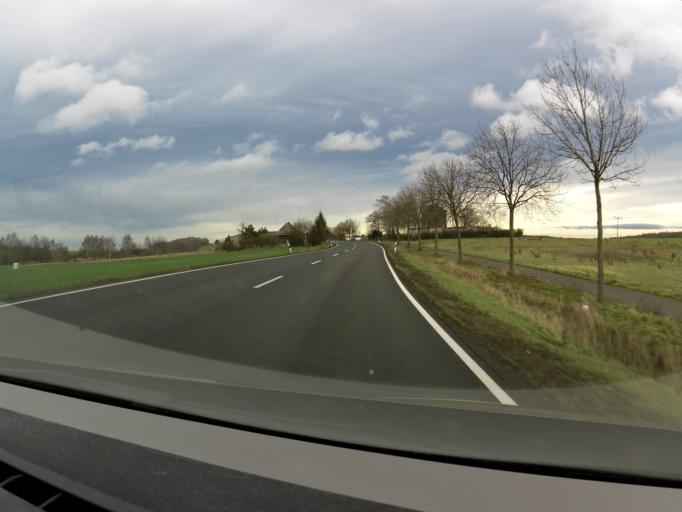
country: DE
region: Saxony-Anhalt
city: Blankenheim
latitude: 51.5554
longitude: 11.4104
